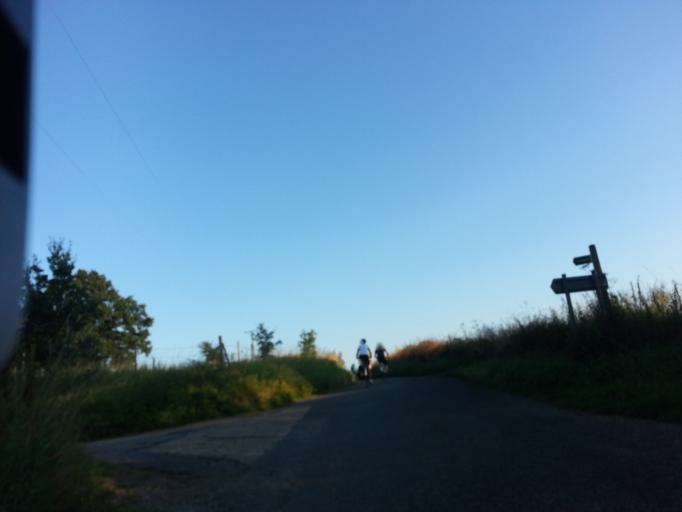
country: GB
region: England
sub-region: Suffolk
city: Kesgrave
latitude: 52.1124
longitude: 1.2340
